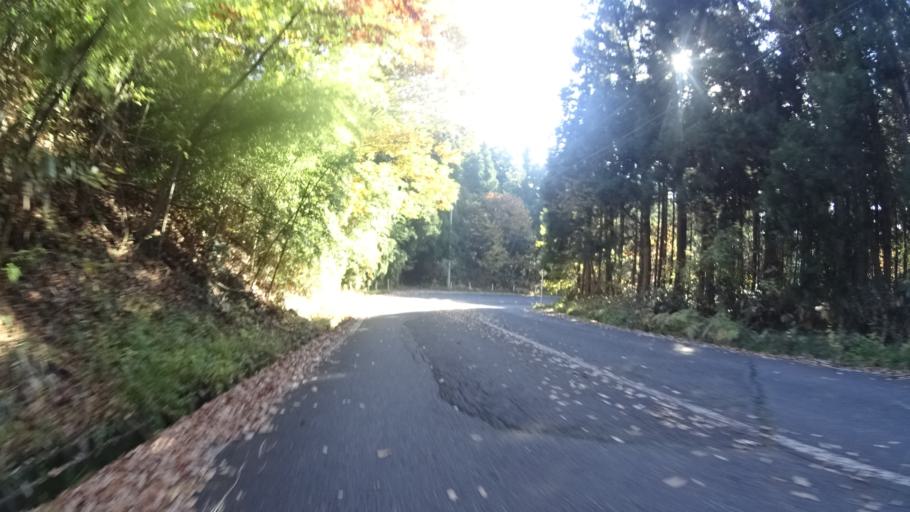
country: JP
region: Niigata
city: Yoshida-kasugacho
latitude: 37.6566
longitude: 138.8127
